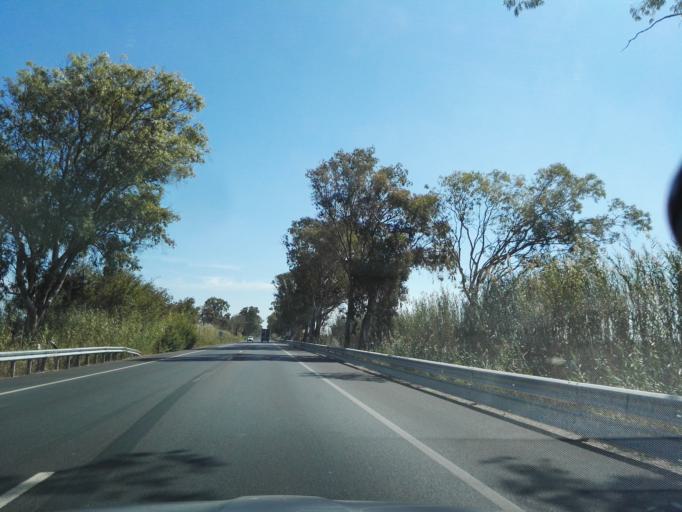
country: PT
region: Santarem
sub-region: Benavente
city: Samora Correia
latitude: 38.9359
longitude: -8.9259
